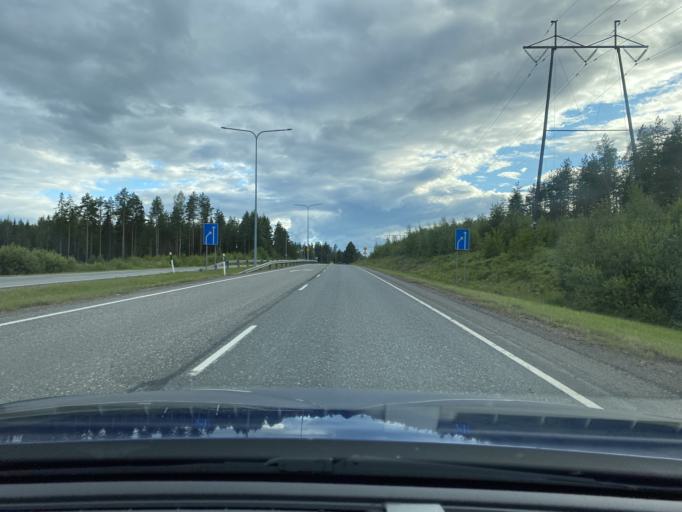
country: FI
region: Haeme
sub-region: Haemeenlinna
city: Haemeenlinna
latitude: 60.9632
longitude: 24.4456
